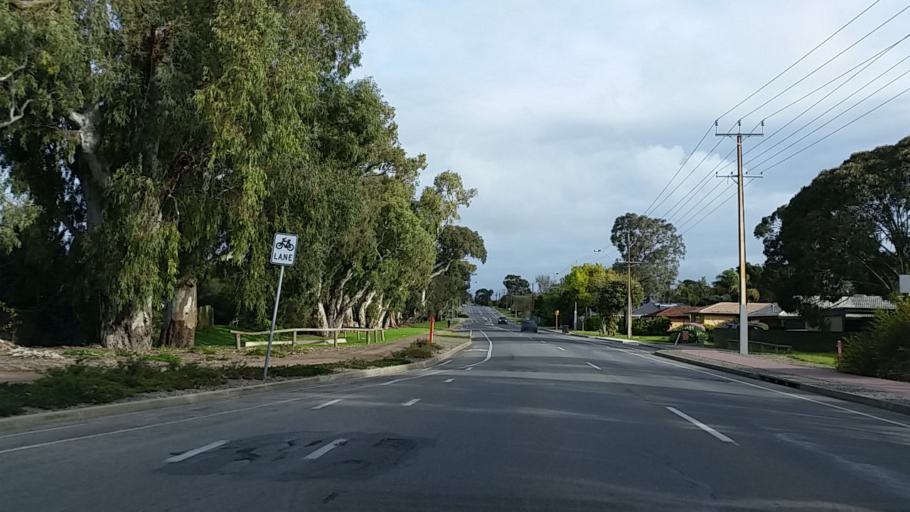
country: AU
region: South Australia
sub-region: Onkaparinga
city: Morphett Vale
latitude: -35.1377
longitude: 138.5373
